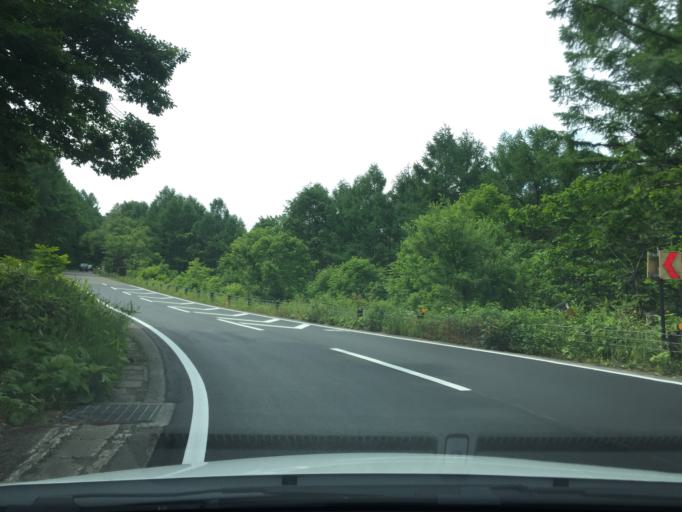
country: JP
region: Fukushima
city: Inawashiro
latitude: 37.6411
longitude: 140.0429
